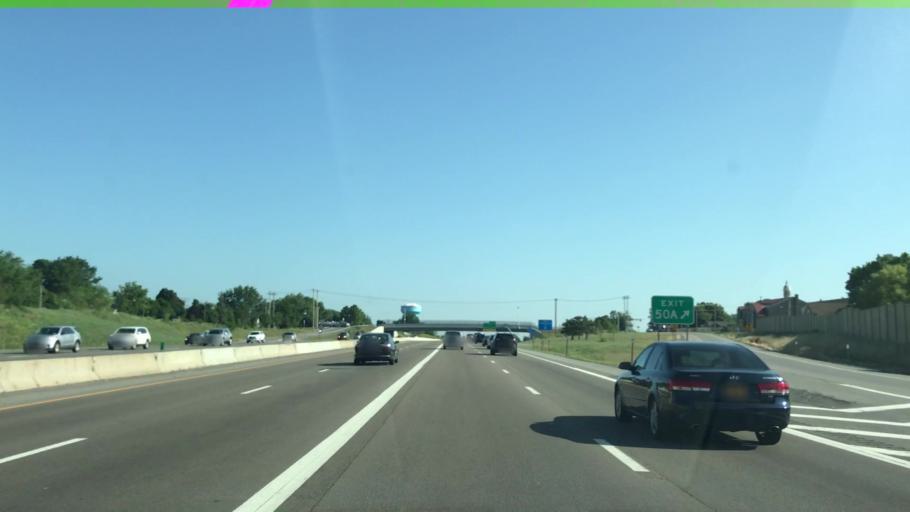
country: US
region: New York
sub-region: Erie County
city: Williamsville
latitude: 42.9417
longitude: -78.7663
